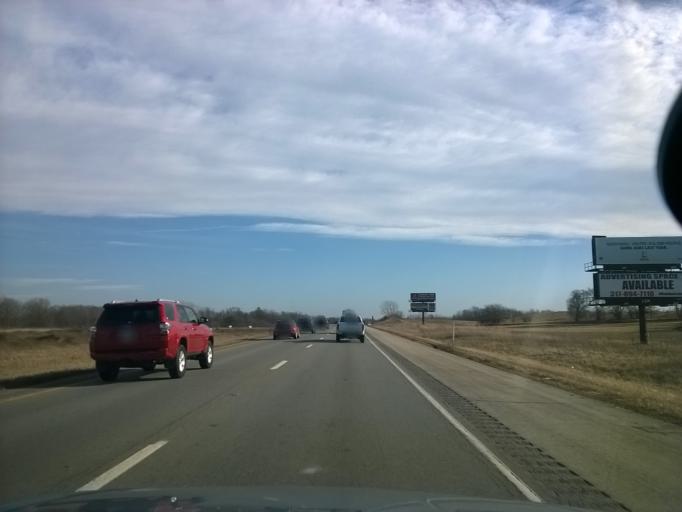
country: US
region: Indiana
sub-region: Johnson County
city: Edinburgh
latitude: 39.4049
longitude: -85.9497
